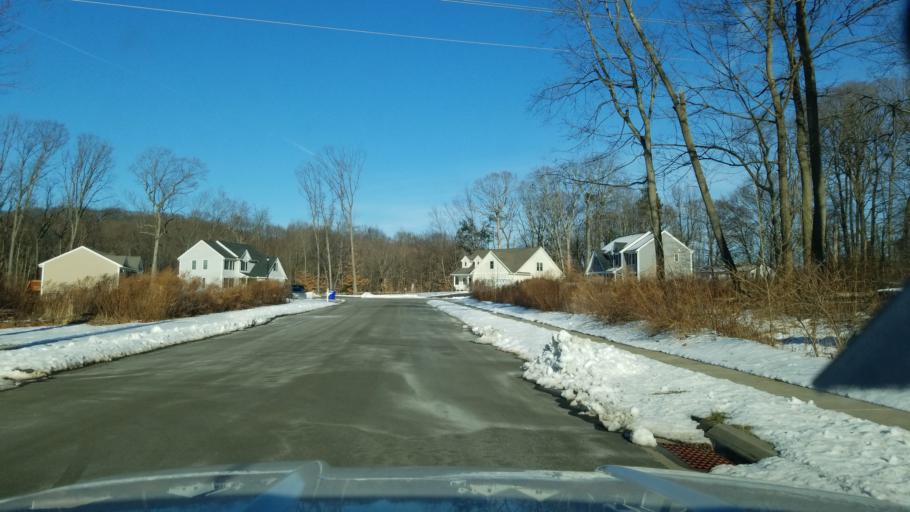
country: US
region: Connecticut
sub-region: New Haven County
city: Wallingford Center
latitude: 41.4345
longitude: -72.8298
